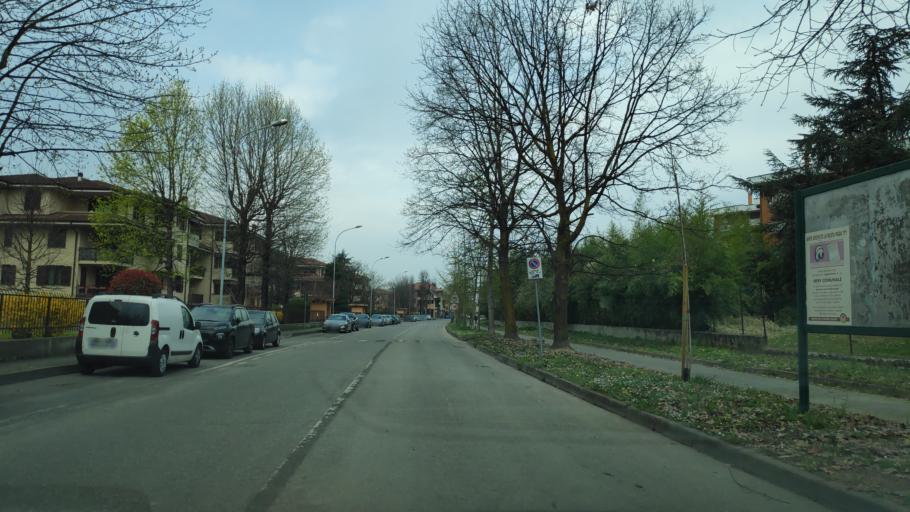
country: IT
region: Lombardy
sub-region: Citta metropolitana di Milano
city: Liscate
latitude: 45.4772
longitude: 9.4113
